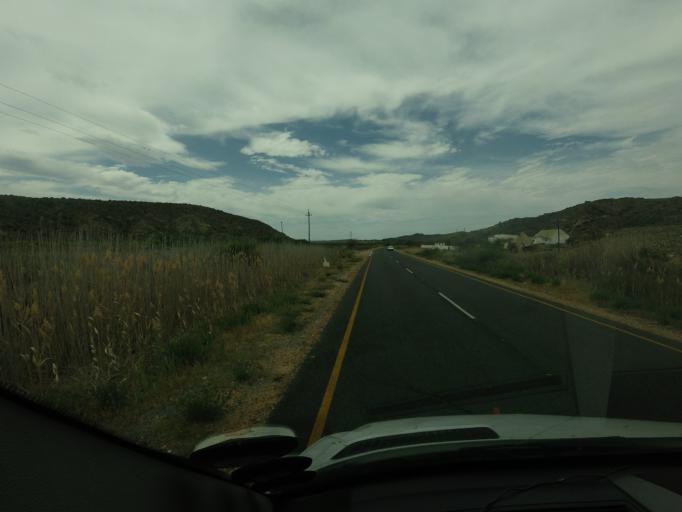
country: ZA
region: Western Cape
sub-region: Overberg District Municipality
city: Swellendam
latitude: -33.8506
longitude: 20.8347
